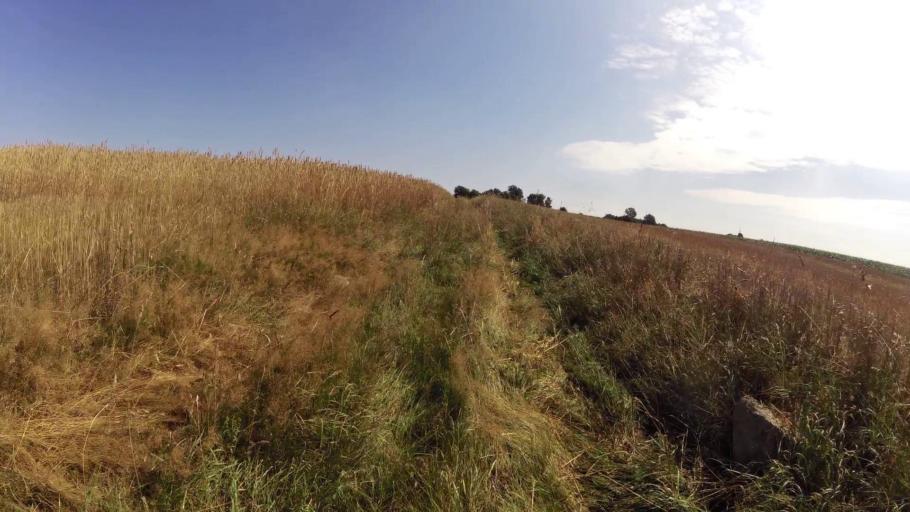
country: PL
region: West Pomeranian Voivodeship
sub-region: Powiat stargardzki
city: Dobrzany
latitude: 53.2817
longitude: 15.4501
